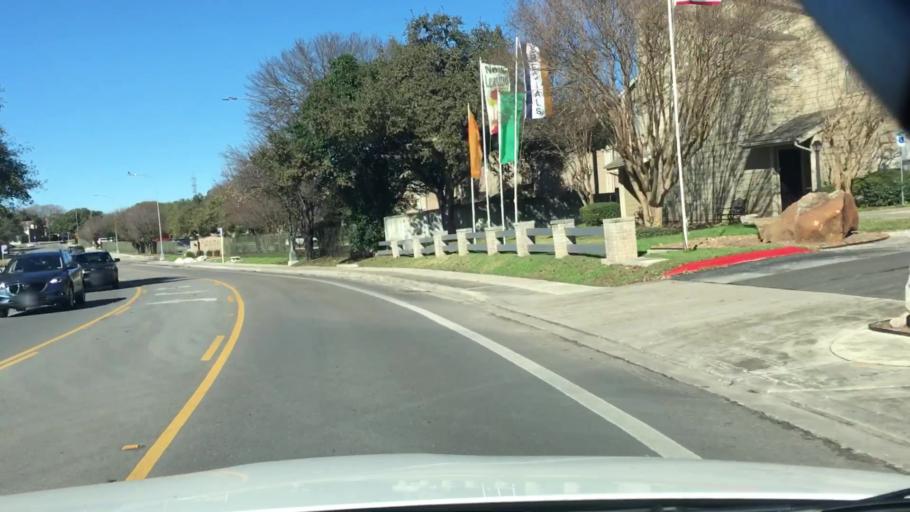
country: US
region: Texas
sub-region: Bexar County
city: Hollywood Park
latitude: 29.5916
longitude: -98.4494
